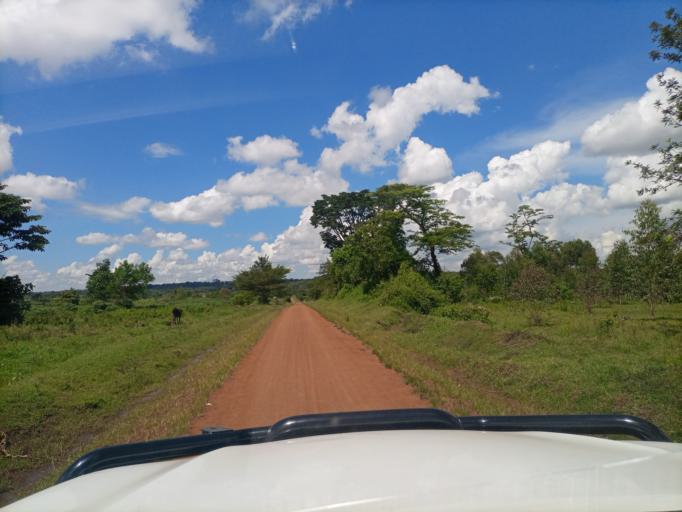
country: UG
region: Eastern Region
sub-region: Tororo District
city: Tororo
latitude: 0.7198
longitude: 34.0158
